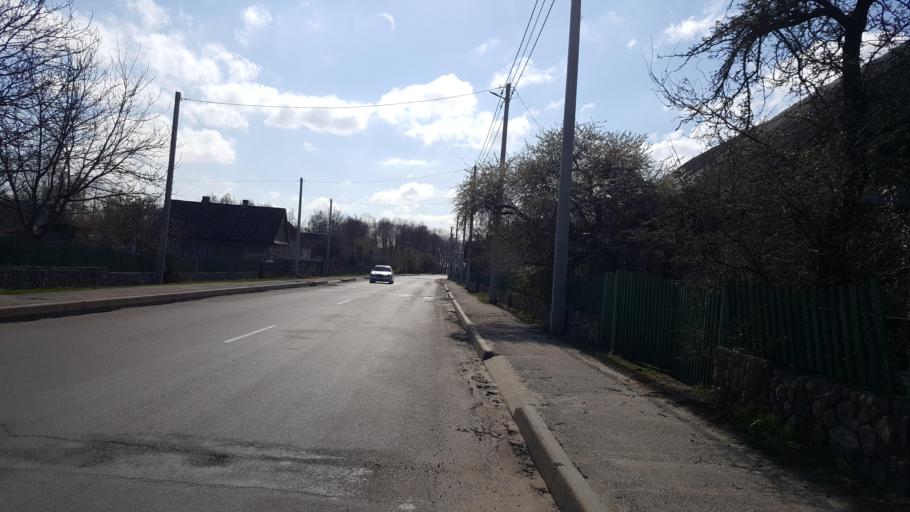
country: BY
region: Brest
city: Kamyanyets
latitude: 52.4026
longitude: 23.8097
